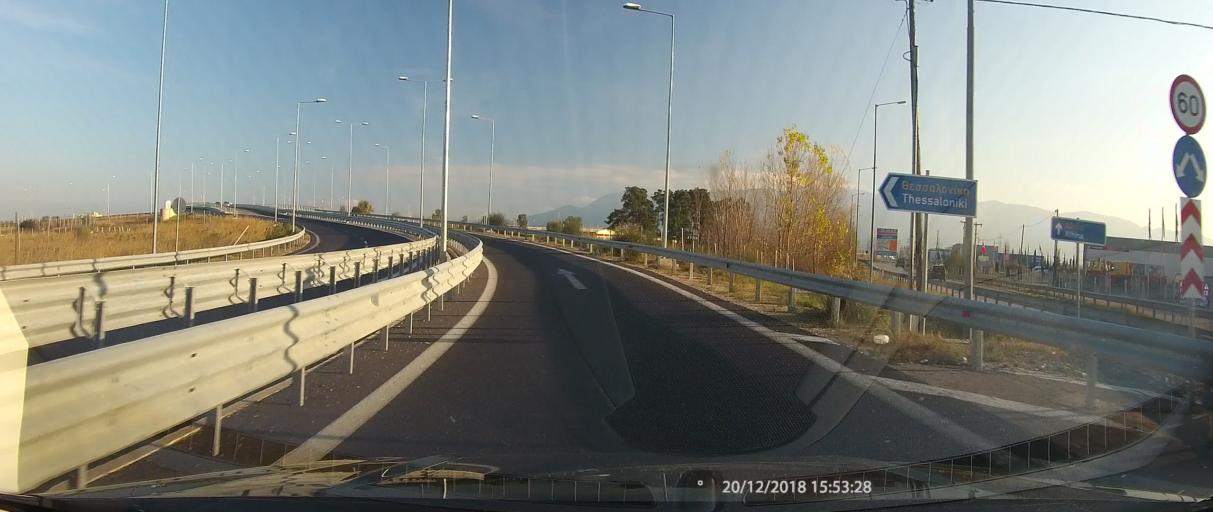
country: GR
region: Central Greece
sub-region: Nomos Fthiotidos
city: Rodhitsa
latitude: 38.8724
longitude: 22.4565
